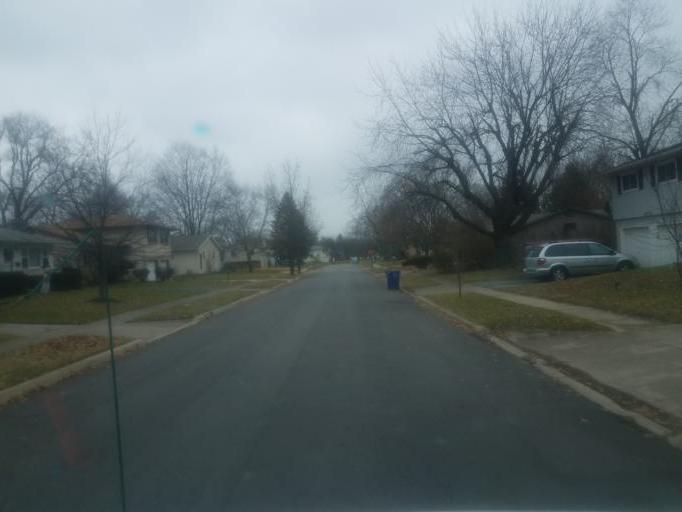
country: US
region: Ohio
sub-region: Franklin County
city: Worthington
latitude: 40.0982
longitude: -82.9819
